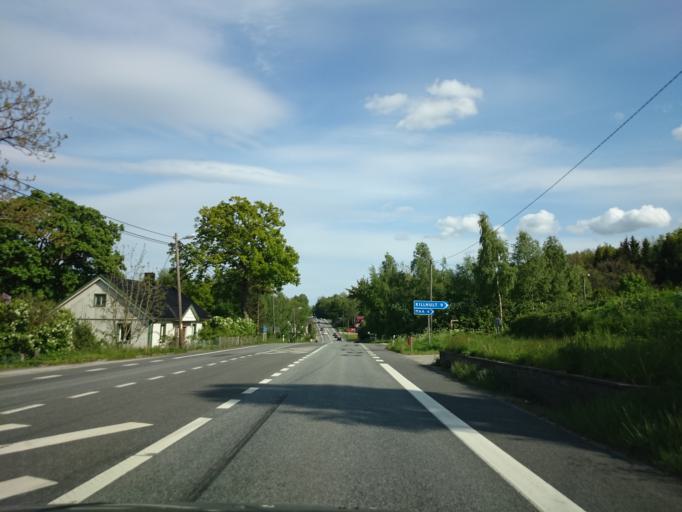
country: SE
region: Skane
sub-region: Kristianstads Kommun
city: Onnestad
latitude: 55.9415
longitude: 13.9033
